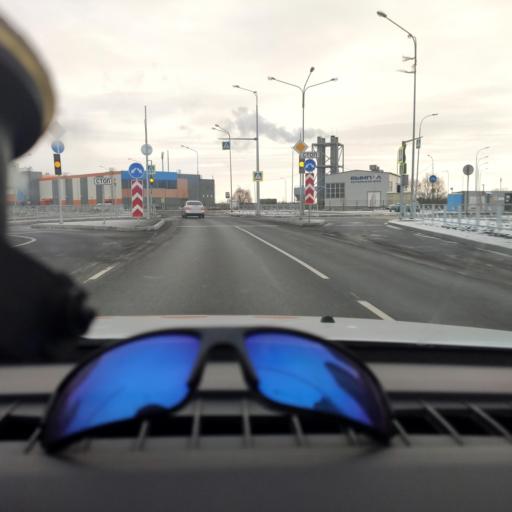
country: RU
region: Samara
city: Samara
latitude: 53.1072
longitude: 50.1380
